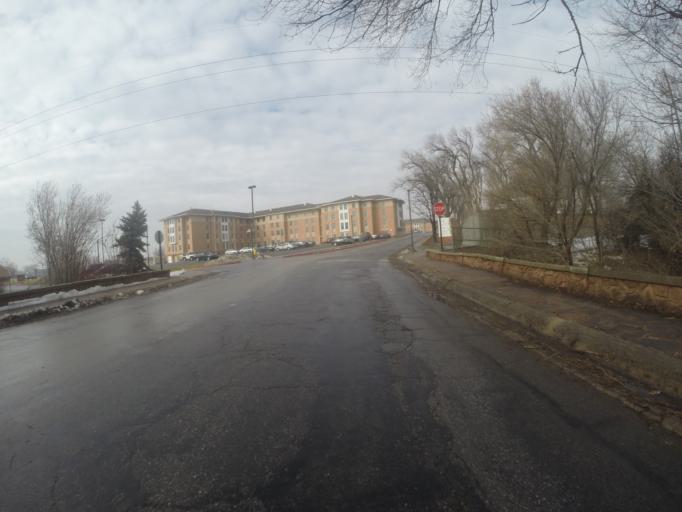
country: US
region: Utah
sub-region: Salt Lake County
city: Canyon Rim
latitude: 40.7627
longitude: -111.8284
